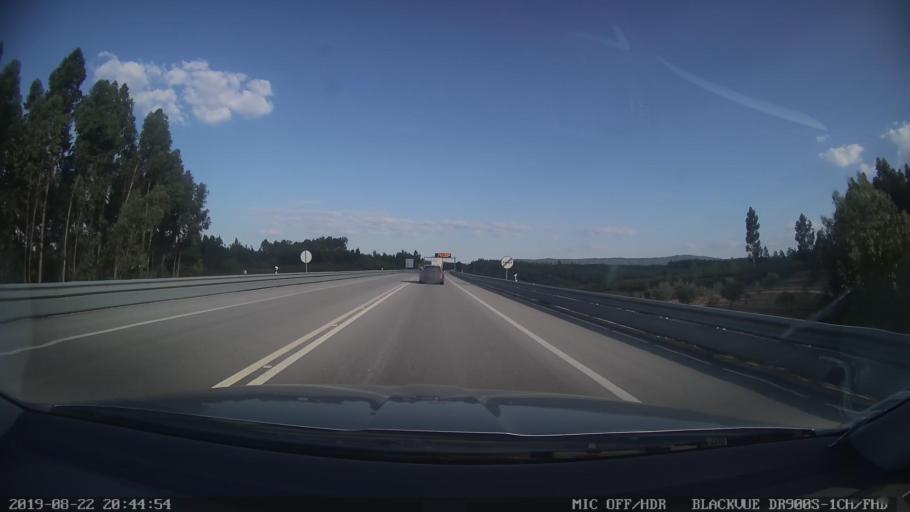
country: PT
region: Castelo Branco
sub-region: Proenca-A-Nova
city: Proenca-a-Nova
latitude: 39.7118
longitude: -7.8582
